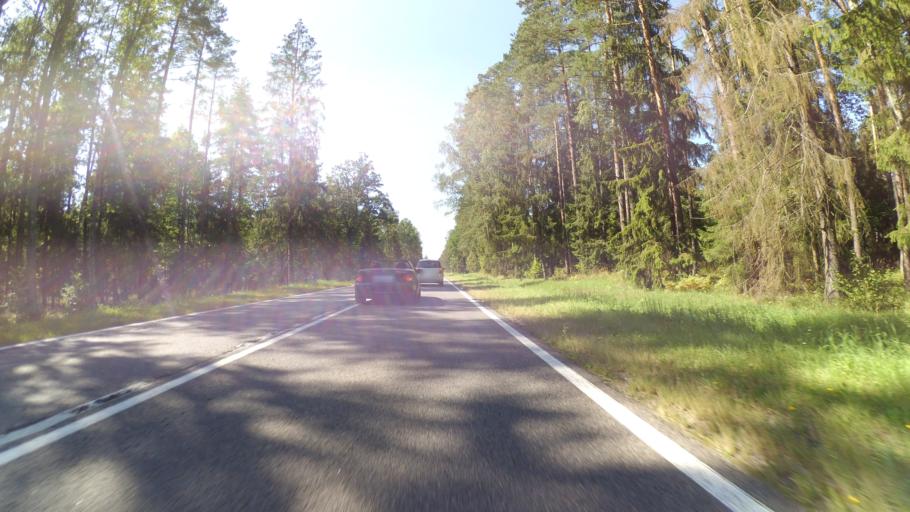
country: PL
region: Podlasie
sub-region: Powiat bialostocki
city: Suprasl
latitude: 53.1310
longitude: 23.4318
